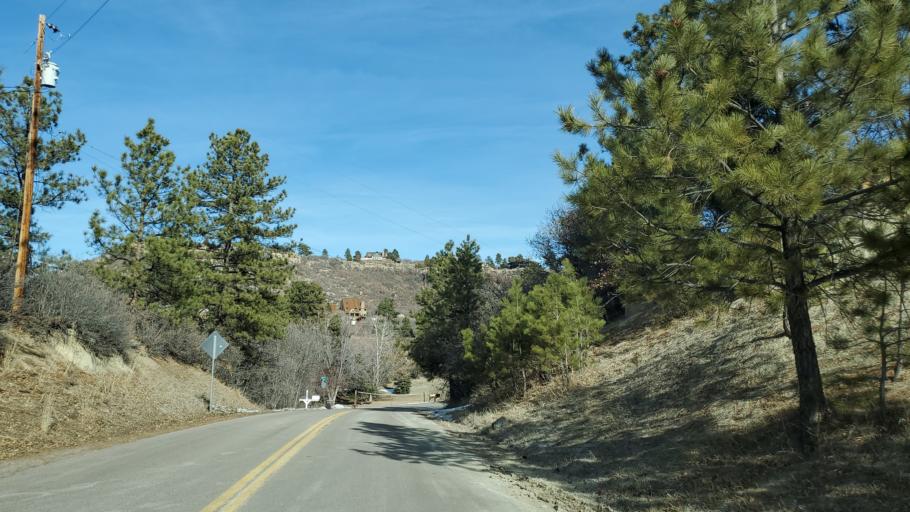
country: US
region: Colorado
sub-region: Douglas County
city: Castle Pines
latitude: 39.4323
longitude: -104.8703
